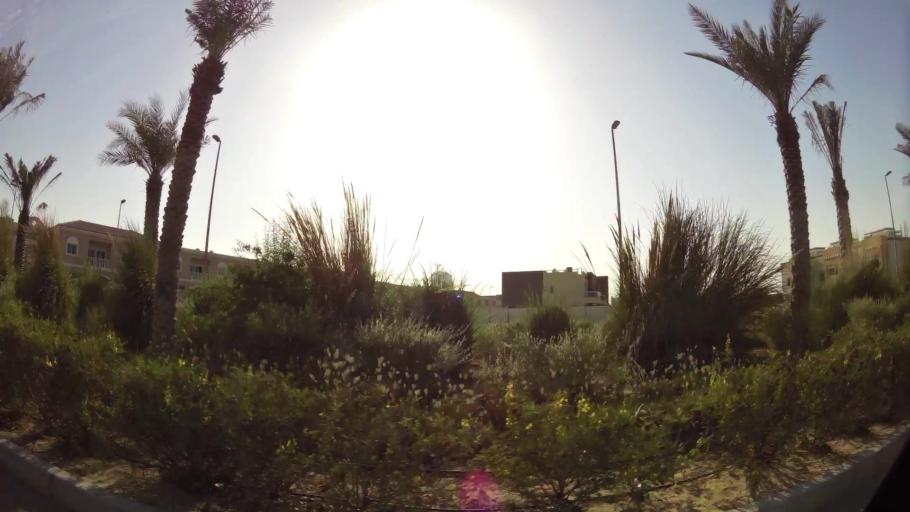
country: AE
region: Dubai
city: Dubai
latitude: 25.0541
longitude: 55.2154
